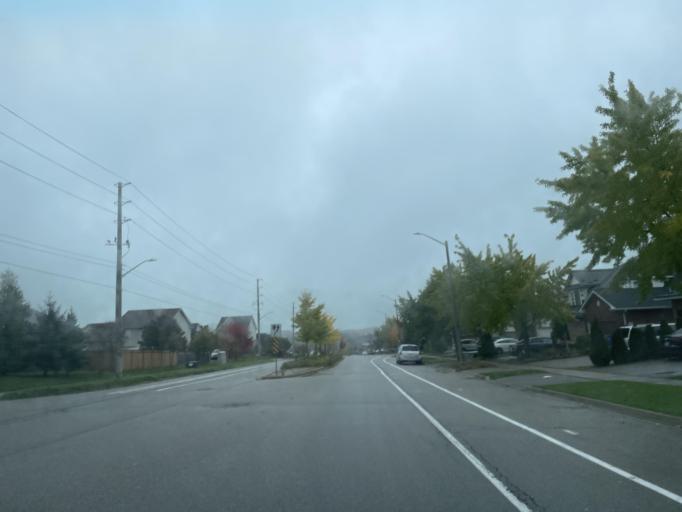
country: CA
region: Ontario
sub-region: Wellington County
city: Guelph
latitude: 43.5665
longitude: -80.2195
